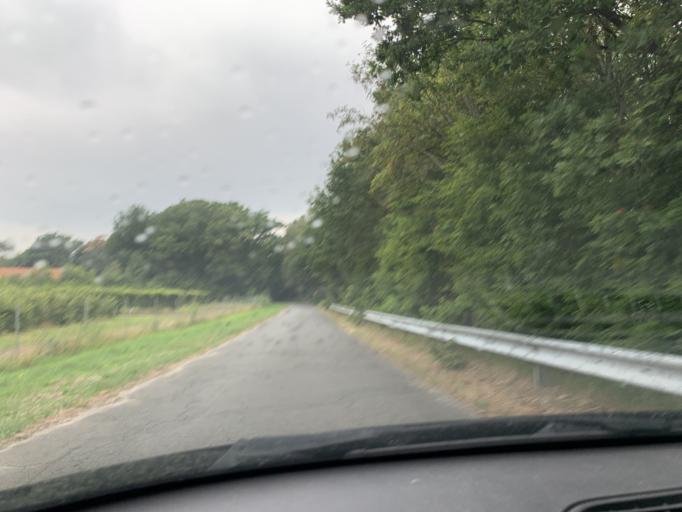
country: DE
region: Lower Saxony
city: Westerstede
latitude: 53.2511
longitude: 7.9852
